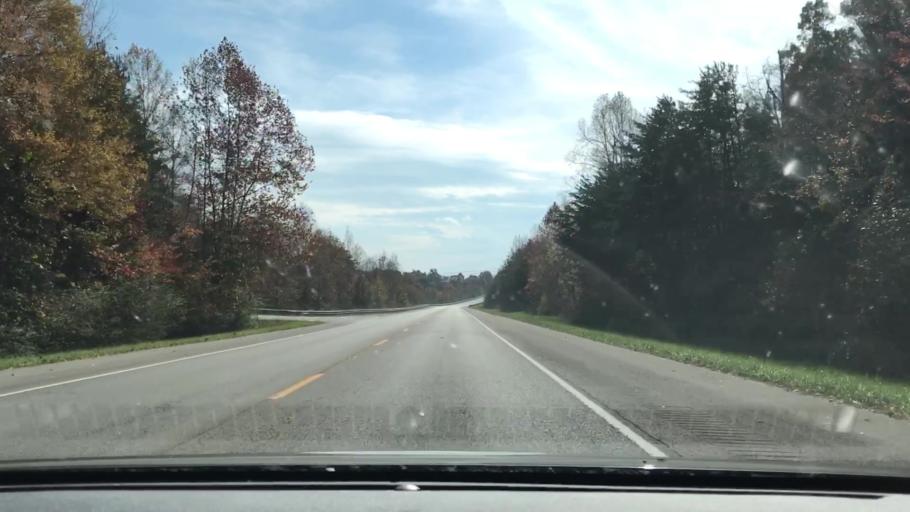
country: US
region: Kentucky
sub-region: McCreary County
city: Pine Knot
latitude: 36.6525
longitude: -84.4357
